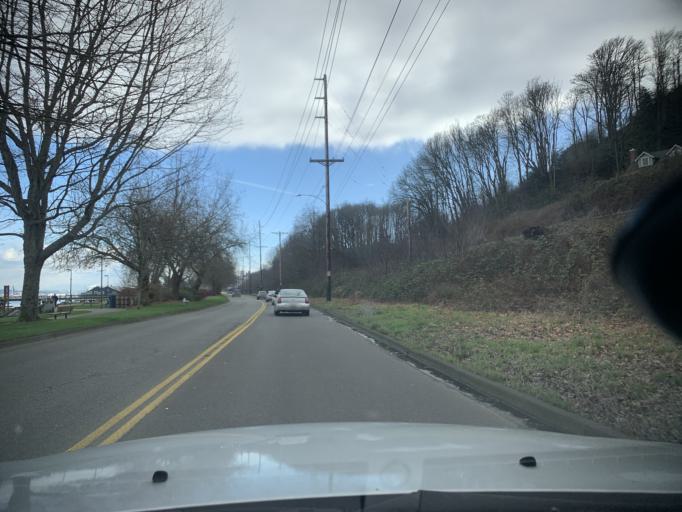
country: US
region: Washington
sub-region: Pierce County
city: Tacoma
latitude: 47.2841
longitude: -122.4847
